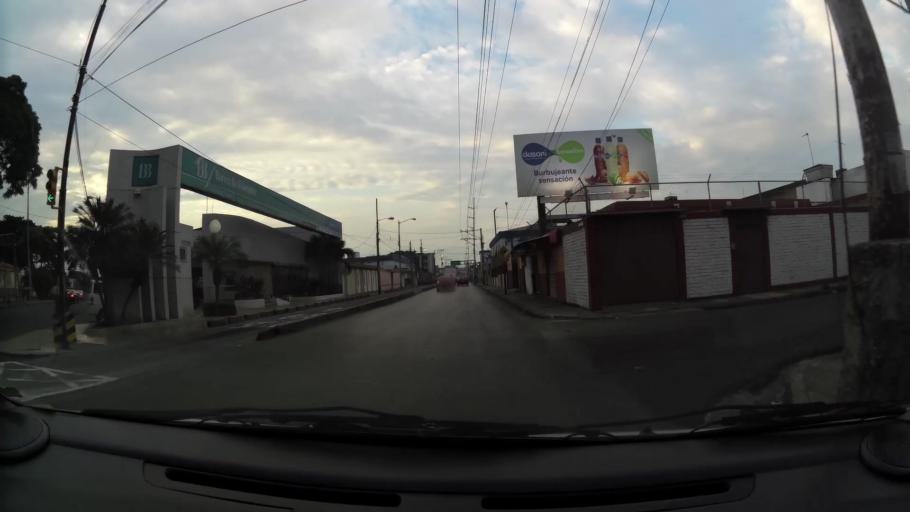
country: EC
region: Guayas
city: Guayaquil
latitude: -2.2263
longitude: -79.8897
